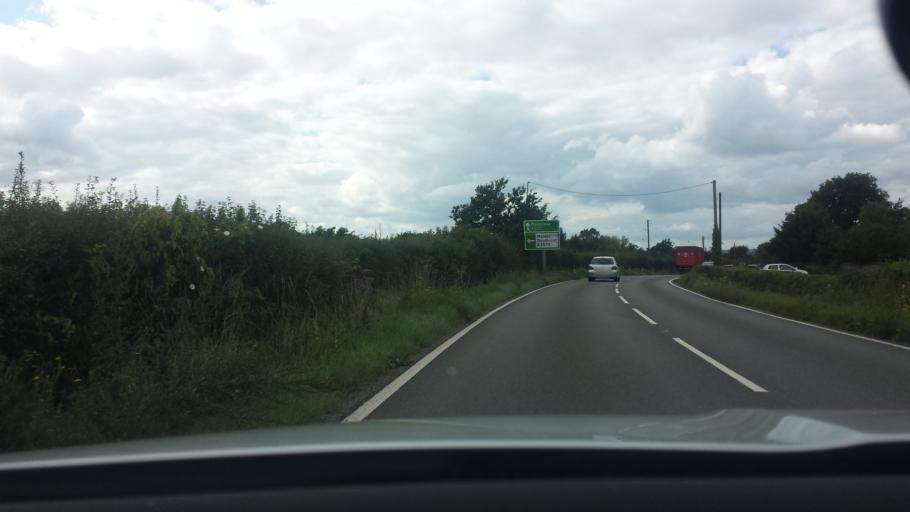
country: GB
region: England
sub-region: Kent
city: Marden
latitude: 51.1988
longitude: 0.5200
